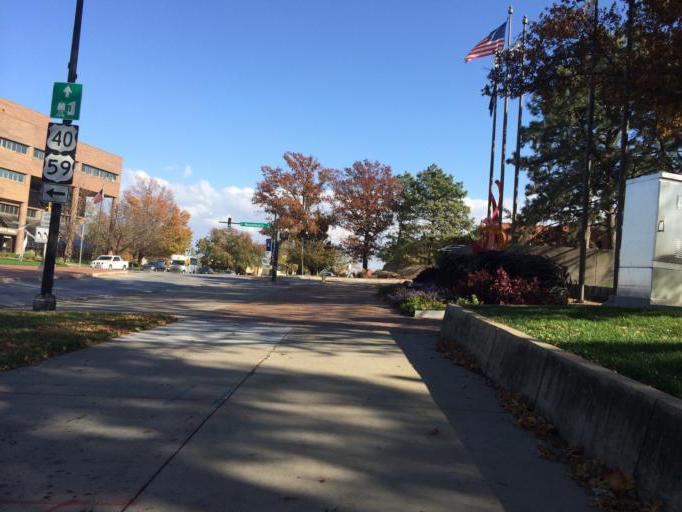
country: US
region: Kansas
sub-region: Douglas County
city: Lawrence
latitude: 38.9729
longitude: -95.2366
